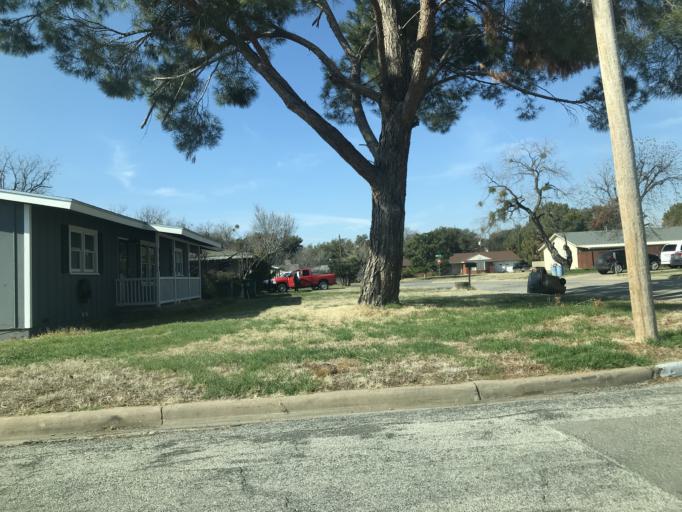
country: US
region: Texas
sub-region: Tom Green County
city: San Angelo
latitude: 31.4294
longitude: -100.4667
